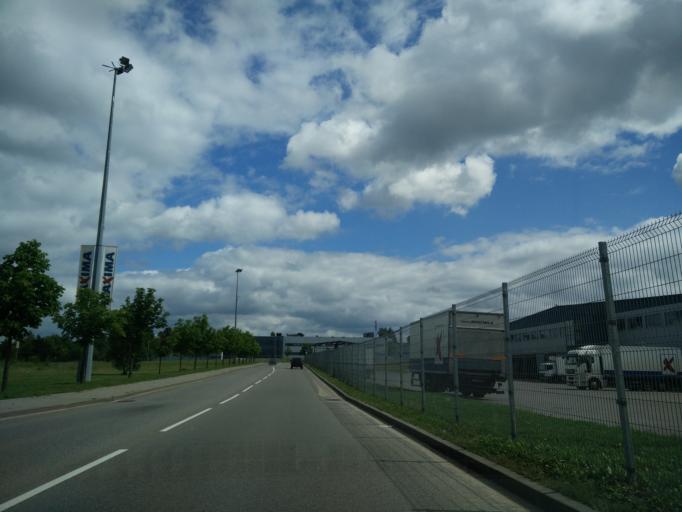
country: LT
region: Vilnius County
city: Pilaite
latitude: 54.6575
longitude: 25.1395
